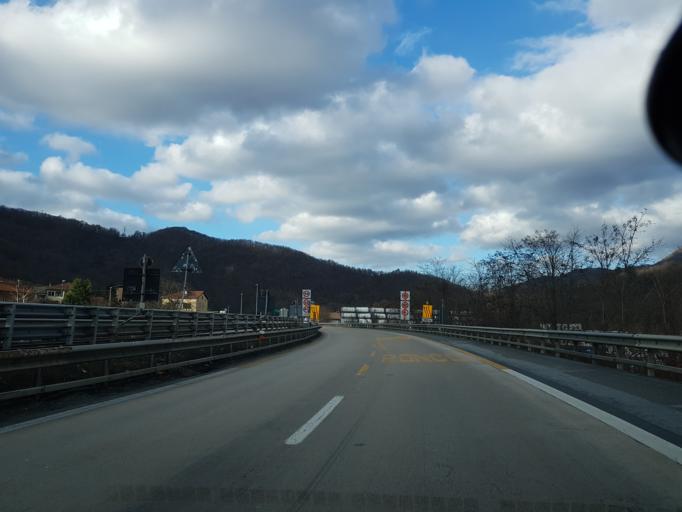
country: IT
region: Liguria
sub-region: Provincia di Genova
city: Ronco Scrivia
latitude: 44.5971
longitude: 8.9546
